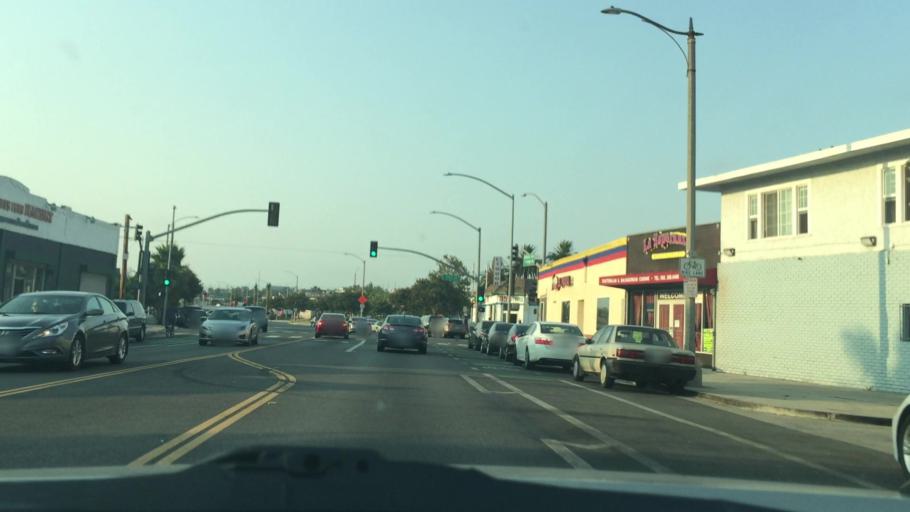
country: US
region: California
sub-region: Los Angeles County
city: Signal Hill
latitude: 33.7875
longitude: -118.1764
